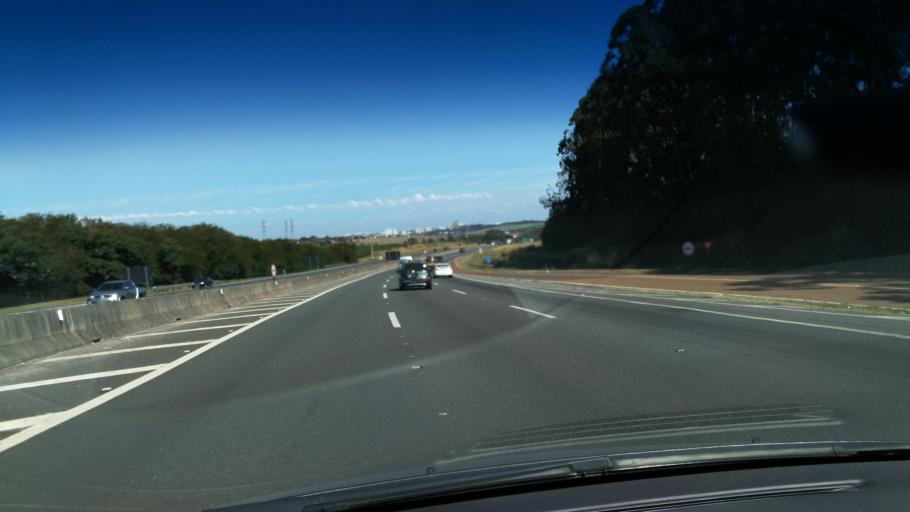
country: BR
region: Sao Paulo
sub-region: Jaguariuna
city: Jaguariuna
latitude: -22.7755
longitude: -47.0227
